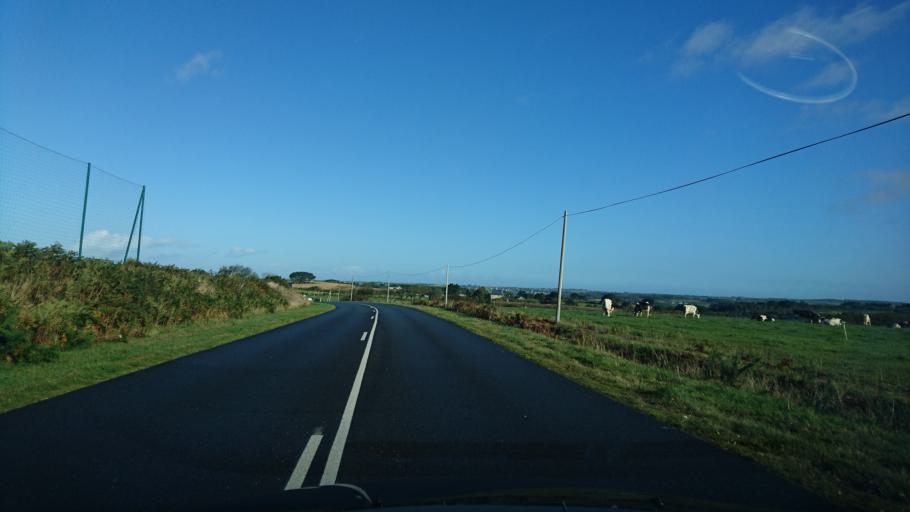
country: FR
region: Brittany
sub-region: Departement du Finistere
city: Plouarzel
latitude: 48.4358
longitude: -4.7156
